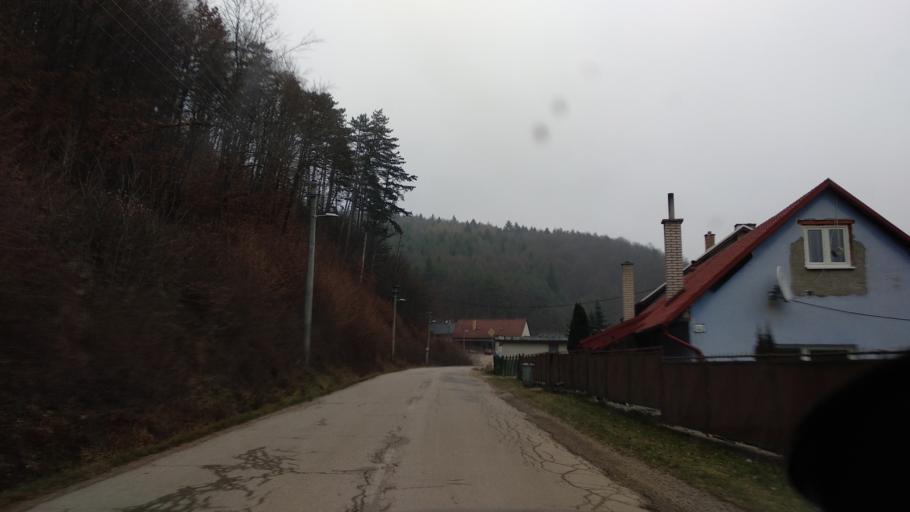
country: SK
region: Nitriansky
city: Trencianske Teplice
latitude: 48.9022
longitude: 18.2671
